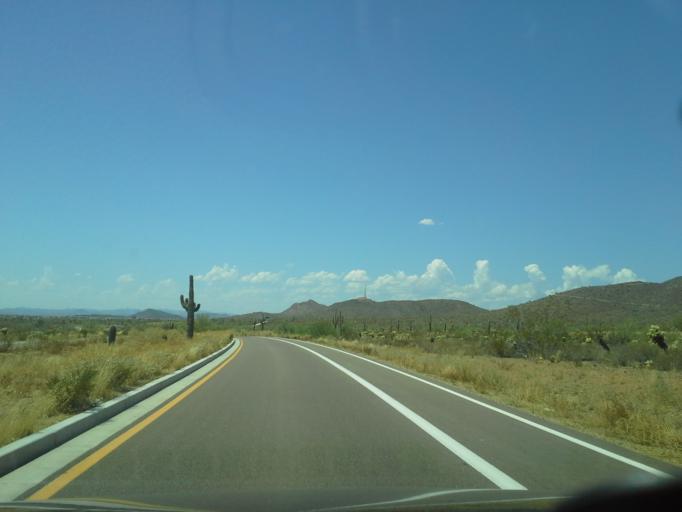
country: US
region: Arizona
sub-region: Maricopa County
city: Anthem
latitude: 33.7720
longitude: -112.0629
